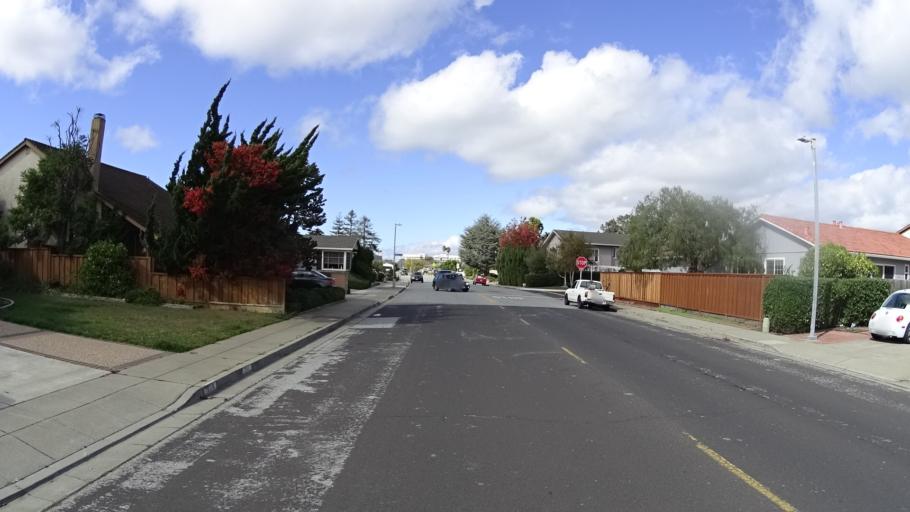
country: US
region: California
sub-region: San Mateo County
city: Foster City
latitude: 37.5660
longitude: -122.2572
